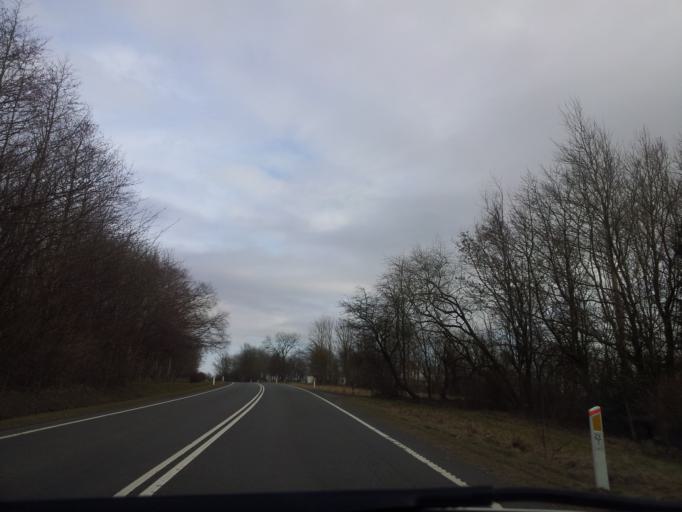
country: DK
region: South Denmark
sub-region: Vejen Kommune
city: Brorup
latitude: 55.4403
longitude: 9.0655
